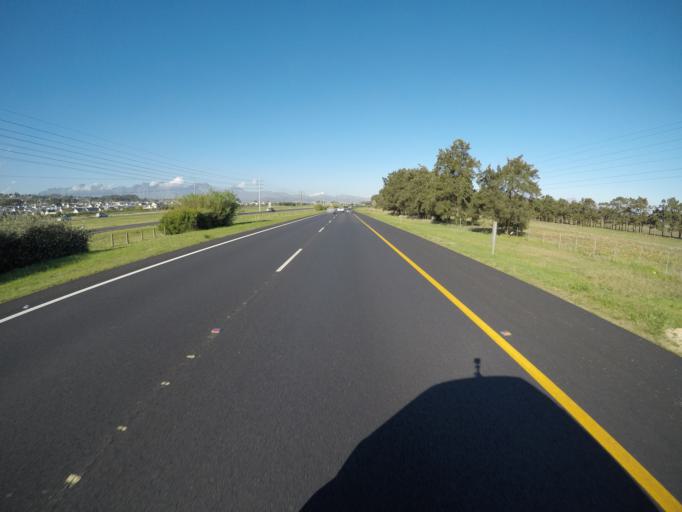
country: ZA
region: Western Cape
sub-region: Cape Winelands District Municipality
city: Stellenbosch
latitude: -34.0684
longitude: 18.8102
